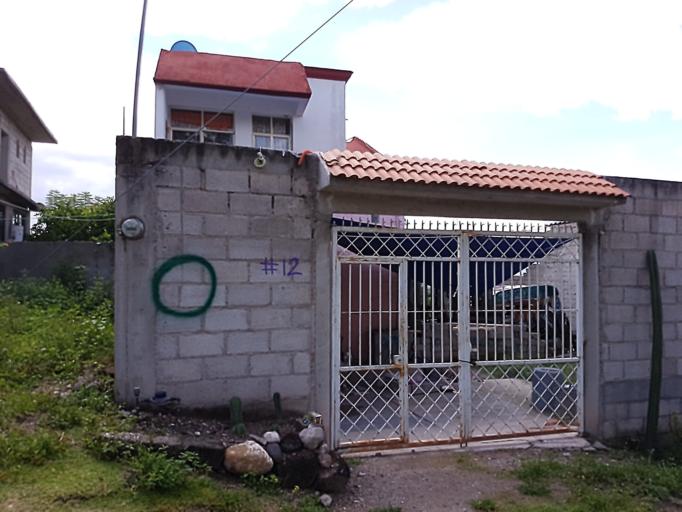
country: MX
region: Oaxaca
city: Ciudad de Huajuapam de Leon
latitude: 17.8056
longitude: -97.7975
